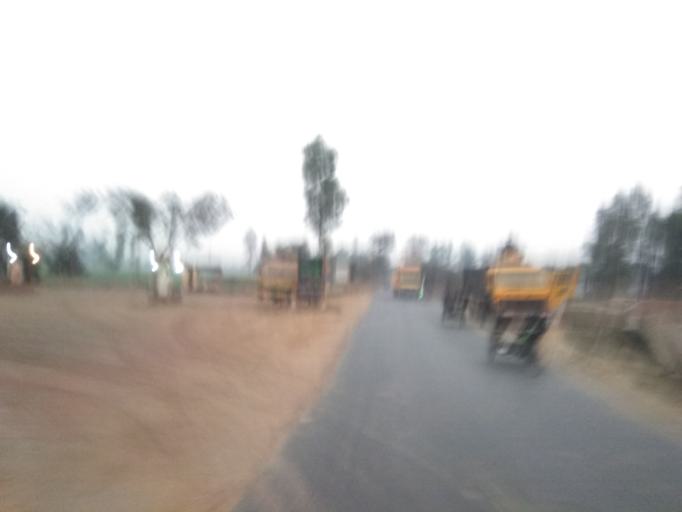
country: BD
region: Rajshahi
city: Bogra
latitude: 24.7387
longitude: 89.3313
